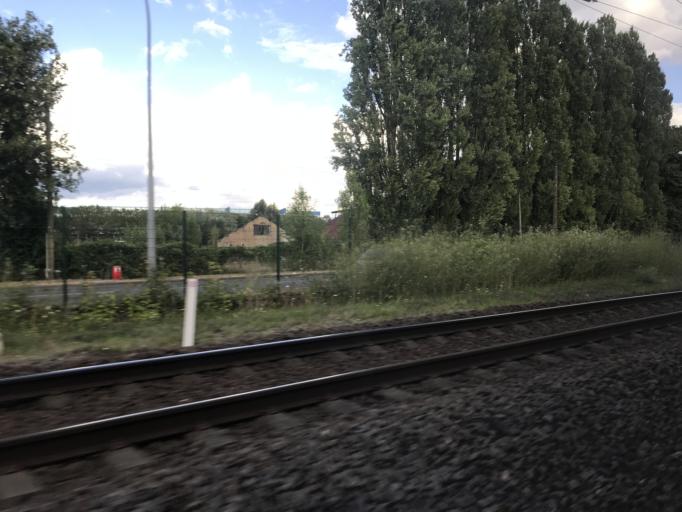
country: FR
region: Champagne-Ardenne
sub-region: Departement des Ardennes
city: Sedan
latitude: 49.6933
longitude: 4.9331
